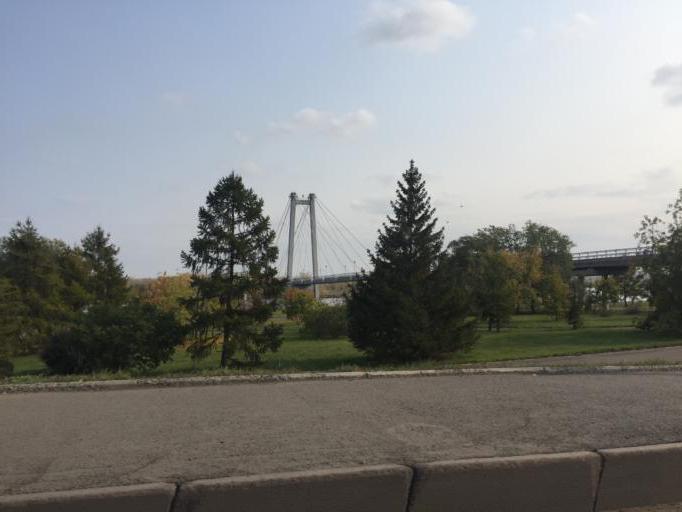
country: RU
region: Krasnoyarskiy
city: Krasnoyarsk
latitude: 56.0140
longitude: 92.8968
